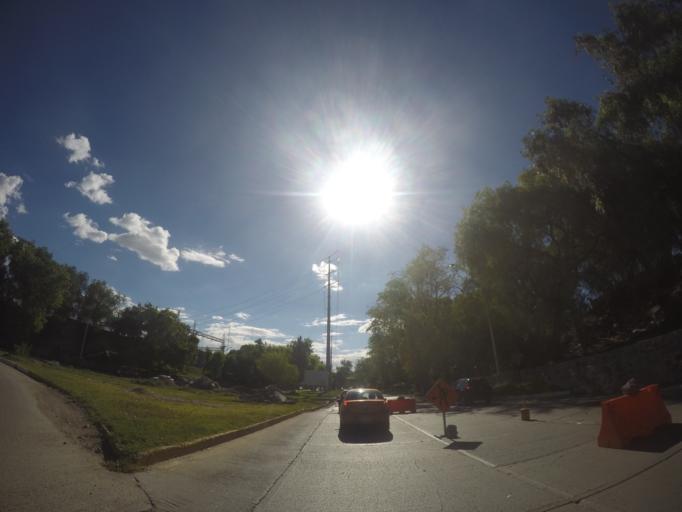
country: MX
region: San Luis Potosi
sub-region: San Luis Potosi
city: San Luis Potosi
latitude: 22.1638
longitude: -100.9892
